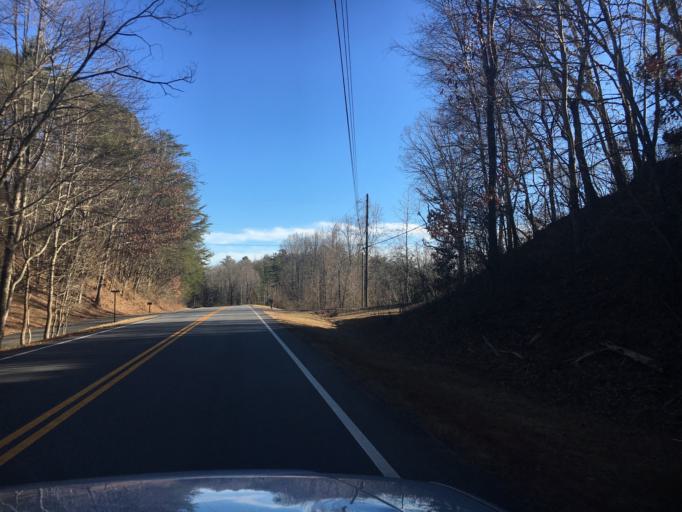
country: US
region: Georgia
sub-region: White County
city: Cleveland
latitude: 34.6636
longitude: -83.8556
